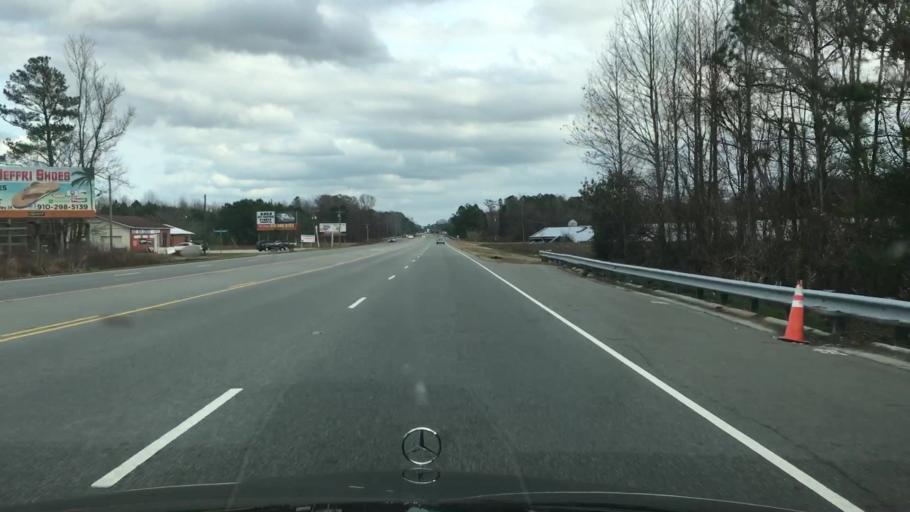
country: US
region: North Carolina
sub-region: Duplin County
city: Beulaville
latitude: 34.9288
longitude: -77.8077
